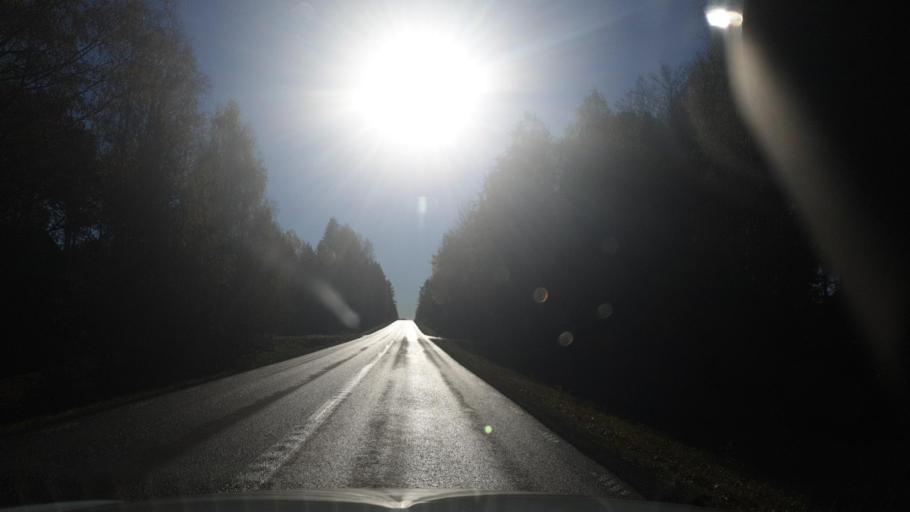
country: SE
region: Vaermland
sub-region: Arvika Kommun
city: Arvika
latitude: 59.5724
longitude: 12.7135
